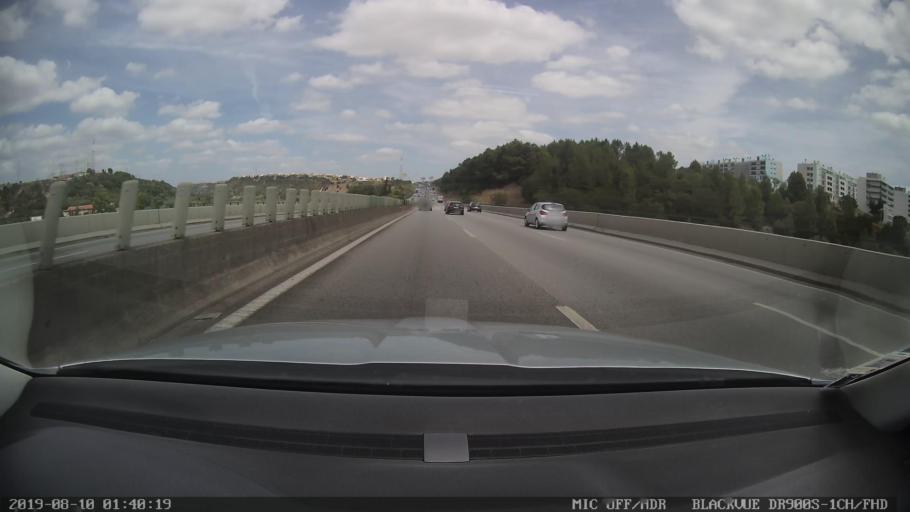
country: PT
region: Lisbon
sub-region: Loures
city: Sacavem
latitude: 38.8008
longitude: -9.1079
